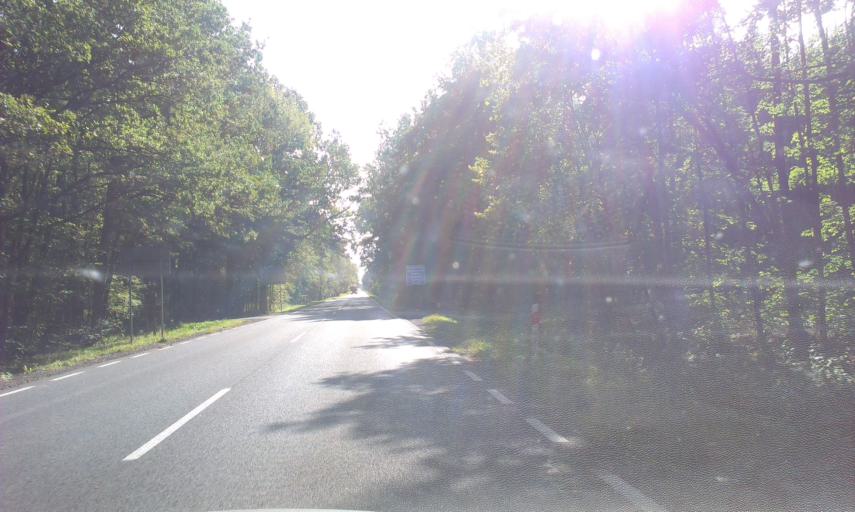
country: PL
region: West Pomeranian Voivodeship
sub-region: Powiat szczecinecki
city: Szczecinek
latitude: 53.6276
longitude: 16.7743
